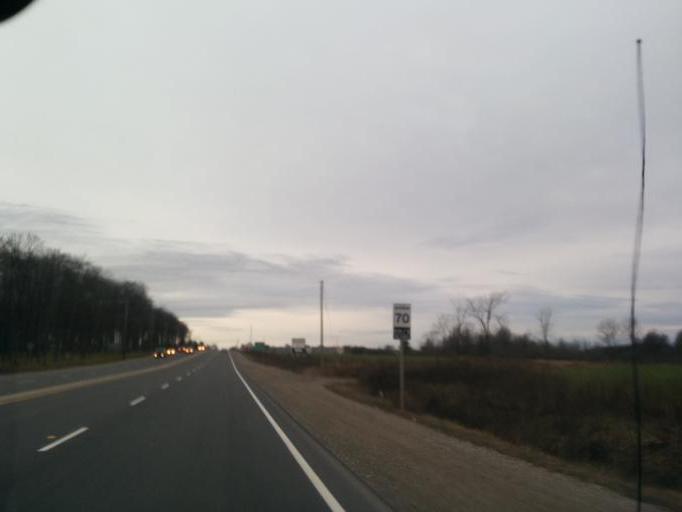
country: CA
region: Ontario
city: Shelburne
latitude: 44.0832
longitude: -80.1805
